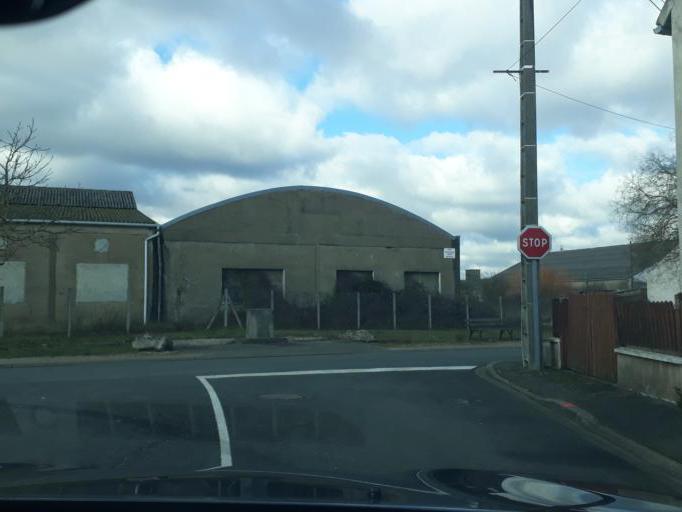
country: FR
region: Centre
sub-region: Departement du Loiret
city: Chevilly
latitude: 48.0316
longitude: 1.8768
